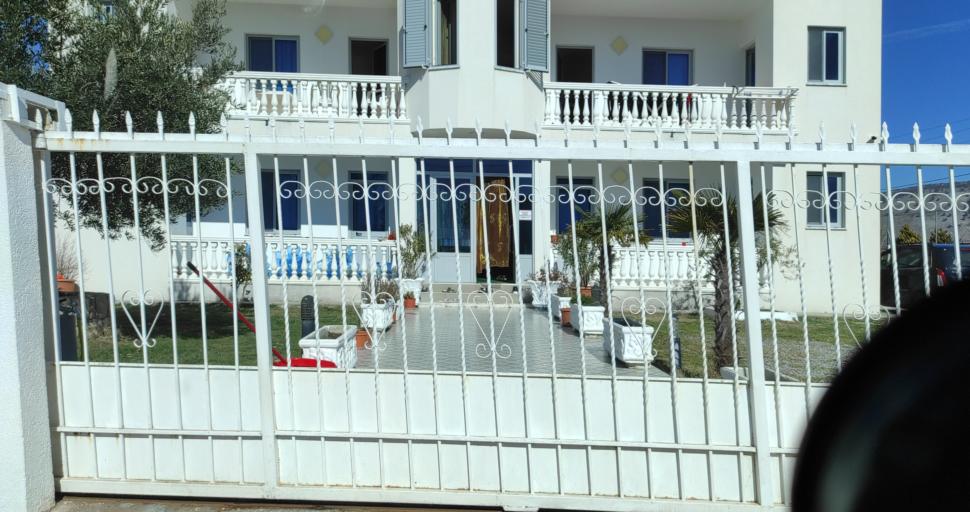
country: AL
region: Shkoder
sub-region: Rrethi i Shkodres
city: Velipoje
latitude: 41.8657
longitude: 19.4339
